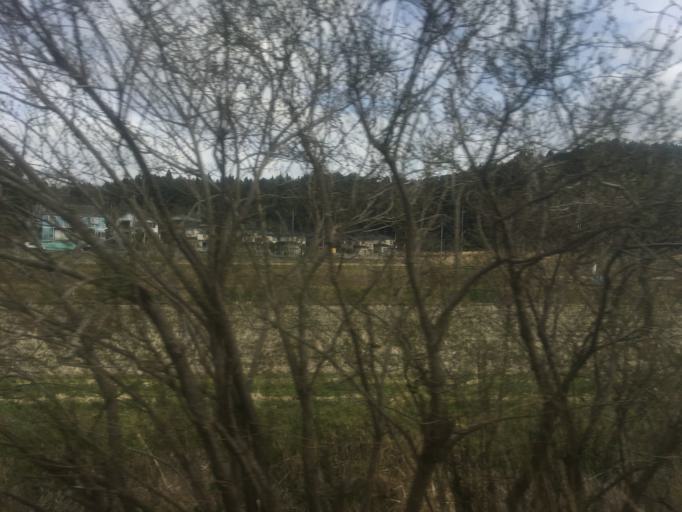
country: JP
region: Chiba
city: Naruto
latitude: 35.6232
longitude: 140.3712
